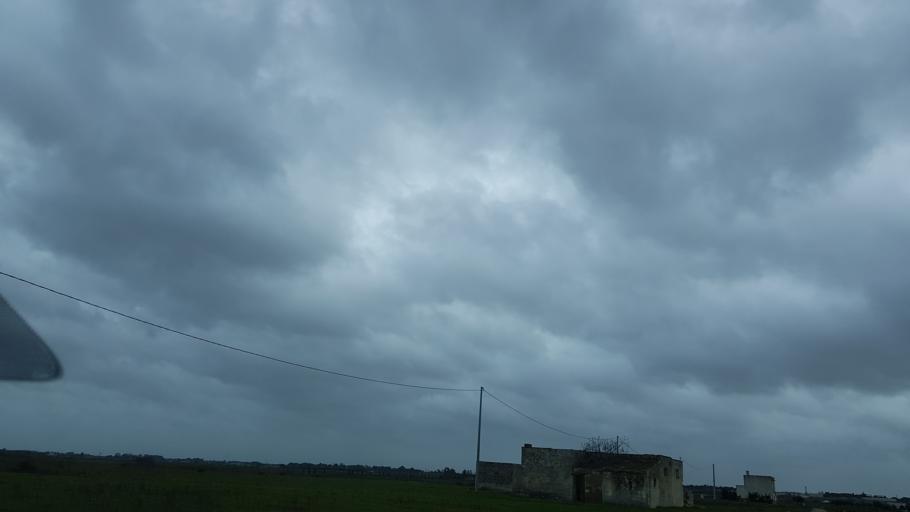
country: IT
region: Apulia
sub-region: Provincia di Brindisi
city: Brindisi
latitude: 40.6604
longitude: 17.8640
